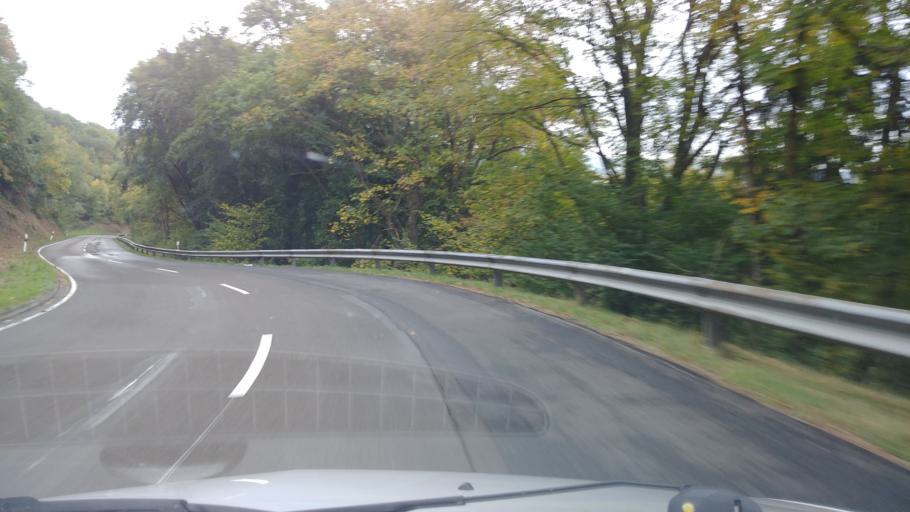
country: DE
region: Rheinland-Pfalz
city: Horath
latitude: 49.8069
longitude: 6.9832
